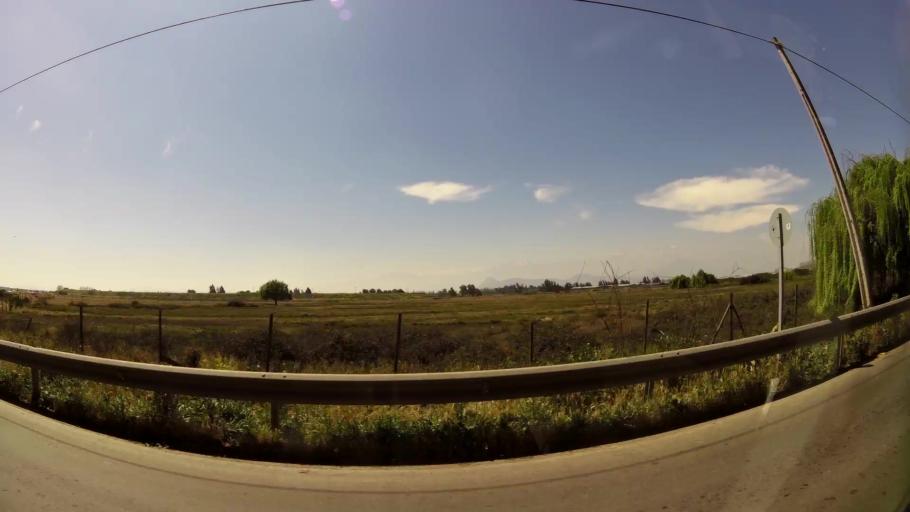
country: CL
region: Santiago Metropolitan
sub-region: Provincia de Santiago
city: Lo Prado
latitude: -33.3750
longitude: -70.7812
